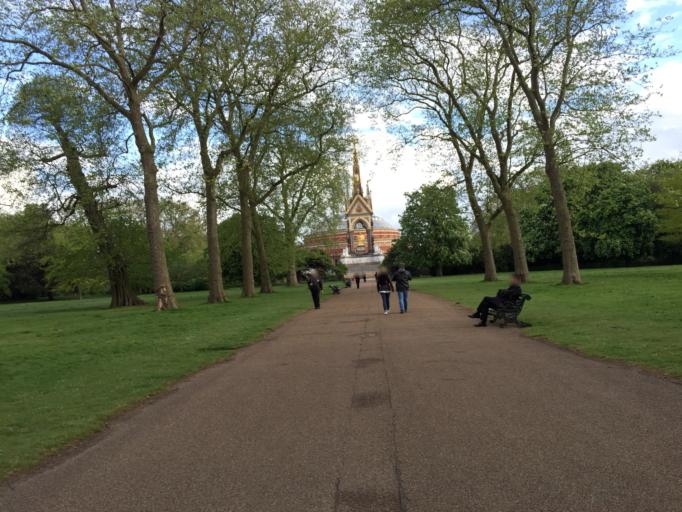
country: GB
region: England
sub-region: Greater London
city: Bayswater
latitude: 51.5042
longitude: -0.1780
